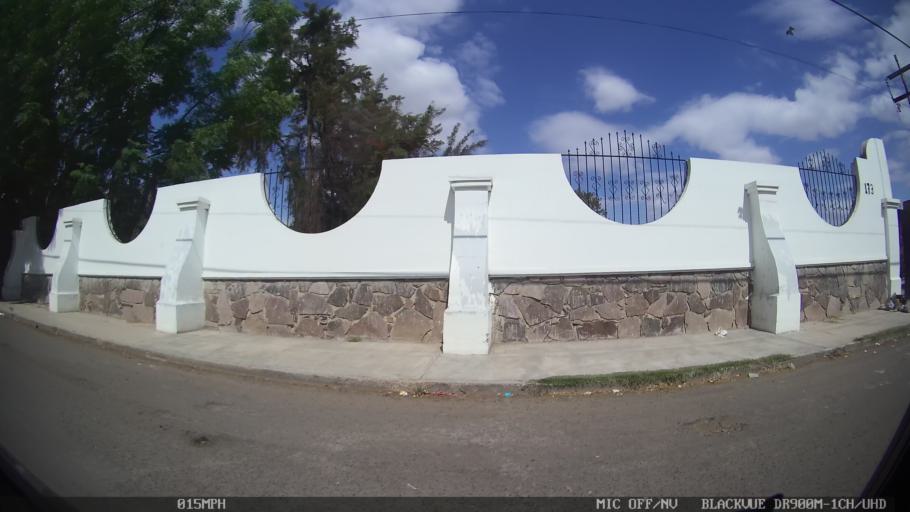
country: MX
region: Jalisco
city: Tonala
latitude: 20.6614
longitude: -103.2442
